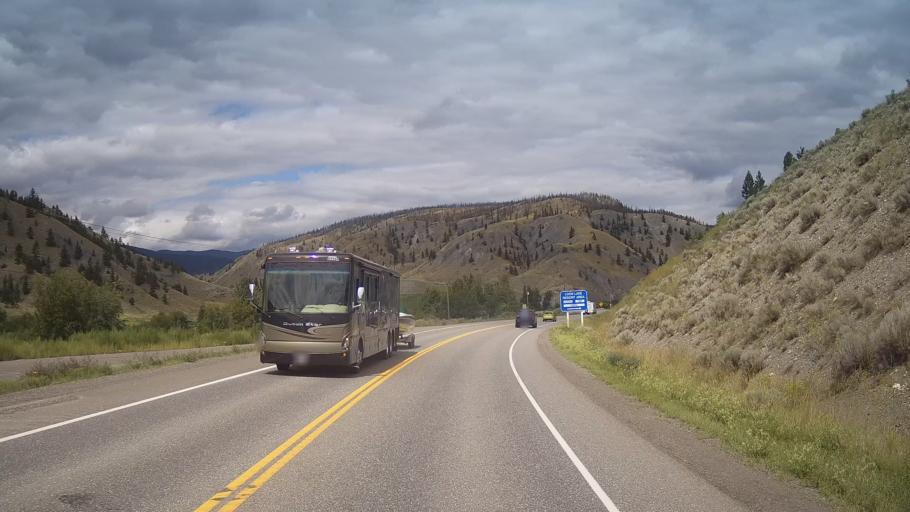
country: CA
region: British Columbia
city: Cache Creek
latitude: 50.9635
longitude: -121.4527
